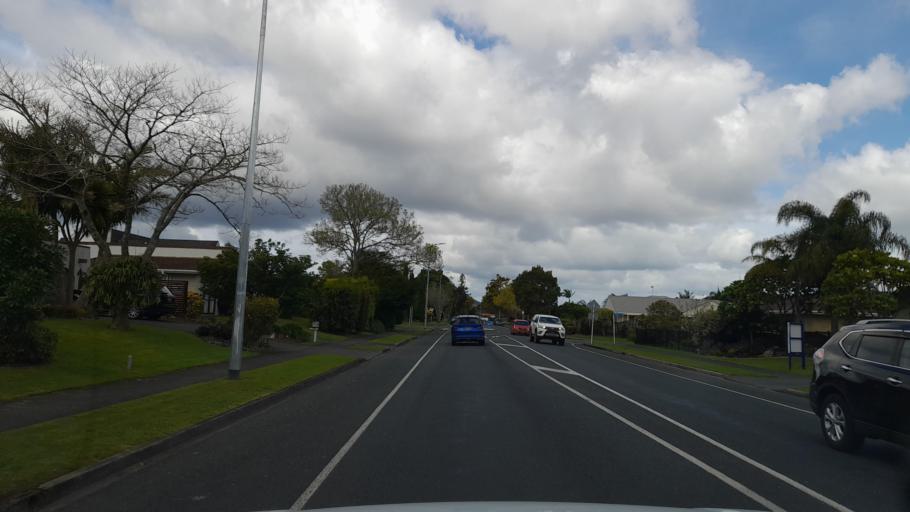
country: NZ
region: Northland
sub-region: Whangarei
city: Whangarei
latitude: -35.6908
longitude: 174.3007
